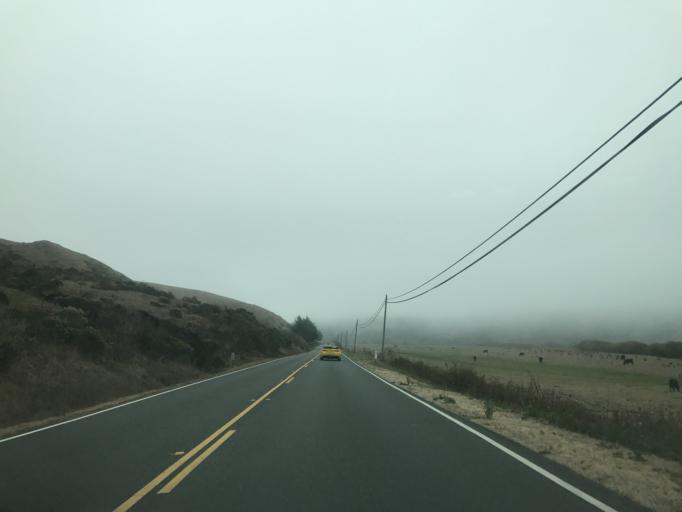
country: US
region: California
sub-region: Sonoma County
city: Monte Rio
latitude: 38.4432
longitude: -123.1101
